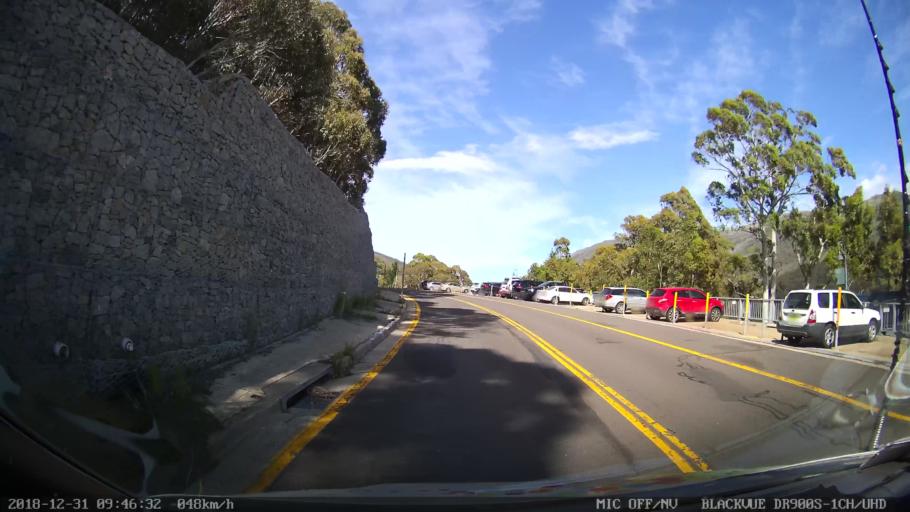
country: AU
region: New South Wales
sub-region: Snowy River
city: Jindabyne
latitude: -36.5042
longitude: 148.3086
